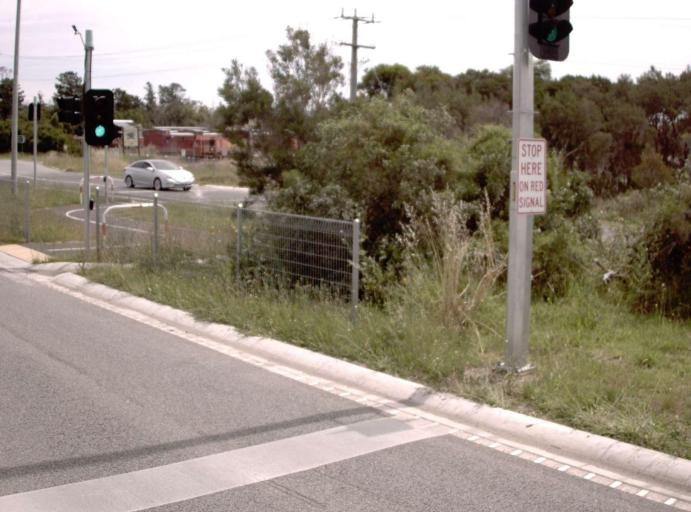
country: AU
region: Victoria
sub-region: Mornington Peninsula
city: Moorooduc
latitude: -38.2133
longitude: 145.1096
